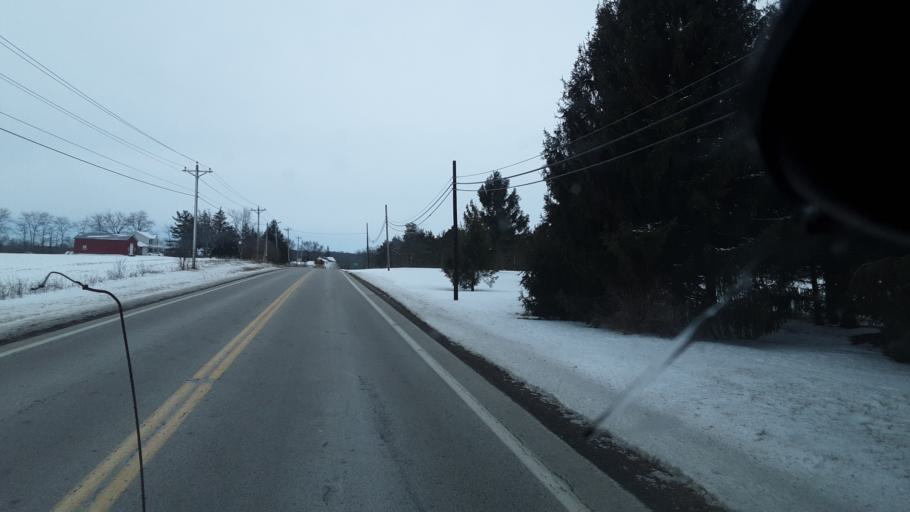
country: US
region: Ohio
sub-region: Union County
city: New California
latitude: 40.1456
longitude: -83.2459
